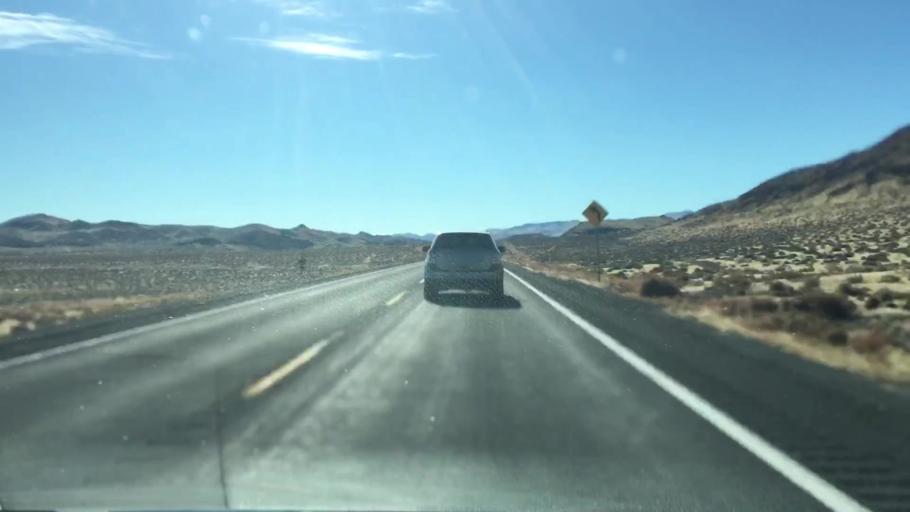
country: US
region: Nevada
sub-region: Lyon County
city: Silver Springs
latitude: 39.3152
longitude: -119.2511
